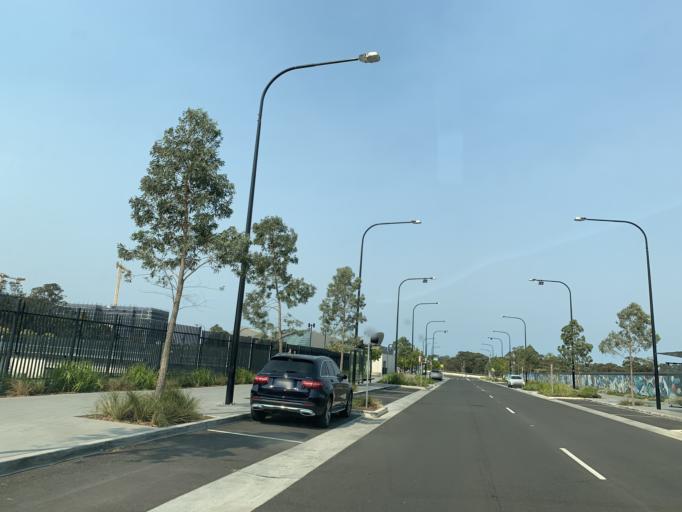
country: AU
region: New South Wales
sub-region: Blacktown
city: Rouse Hill
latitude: -33.6923
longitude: 150.9049
